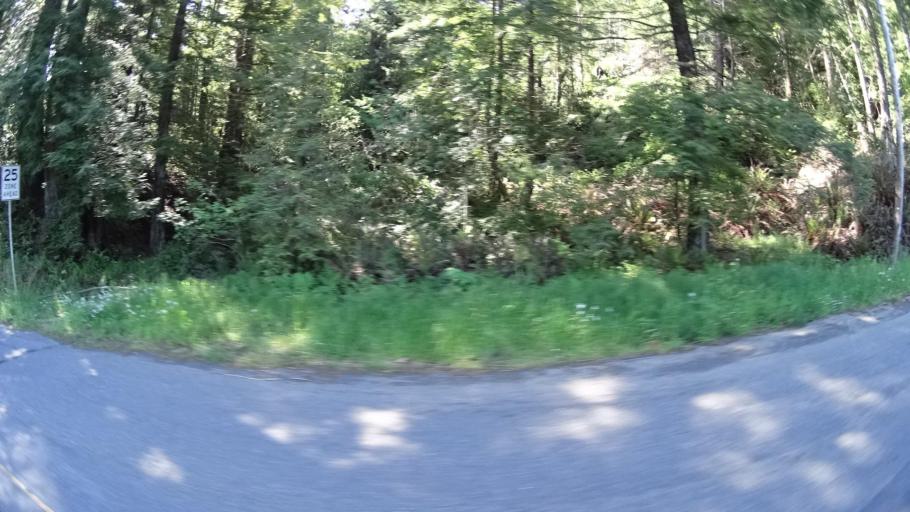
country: US
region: California
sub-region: Humboldt County
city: Rio Dell
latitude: 40.5063
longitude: -124.1299
